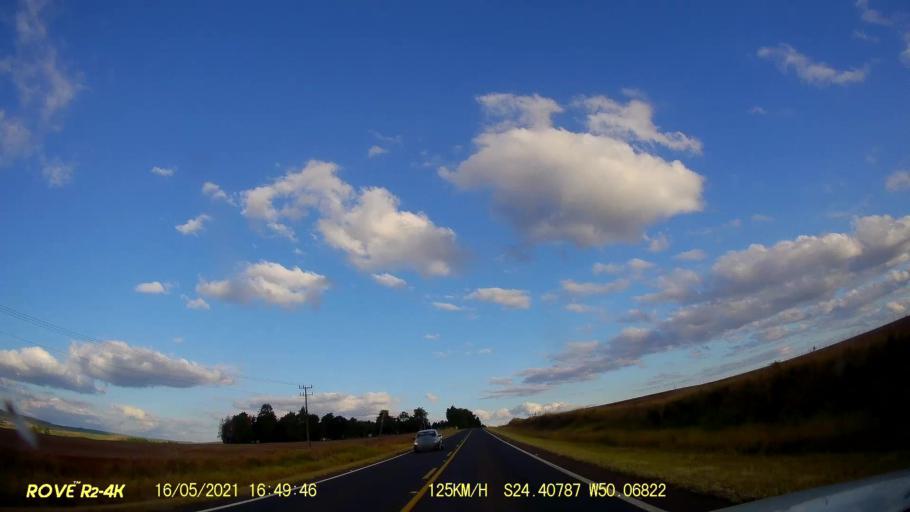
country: BR
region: Parana
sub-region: Pirai Do Sul
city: Pirai do Sul
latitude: -24.4080
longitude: -50.0681
